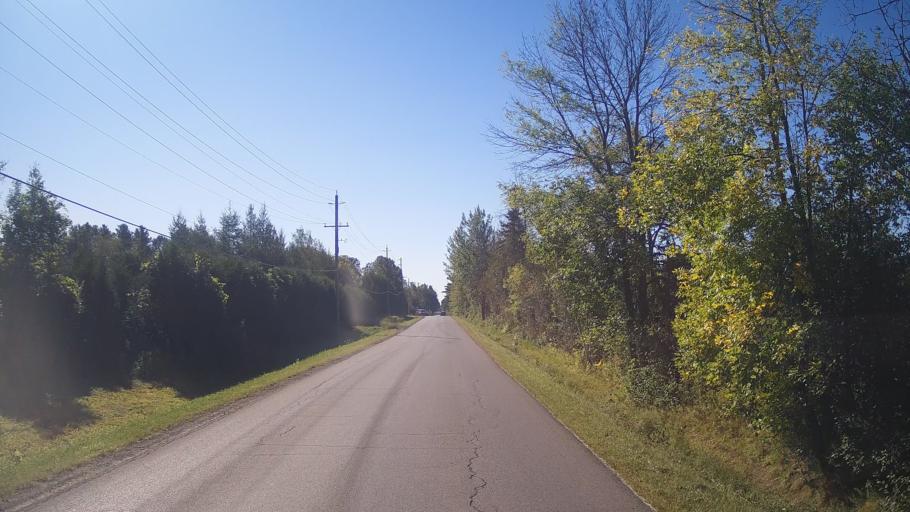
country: CA
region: Ontario
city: Prescott
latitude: 45.0191
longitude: -75.6173
